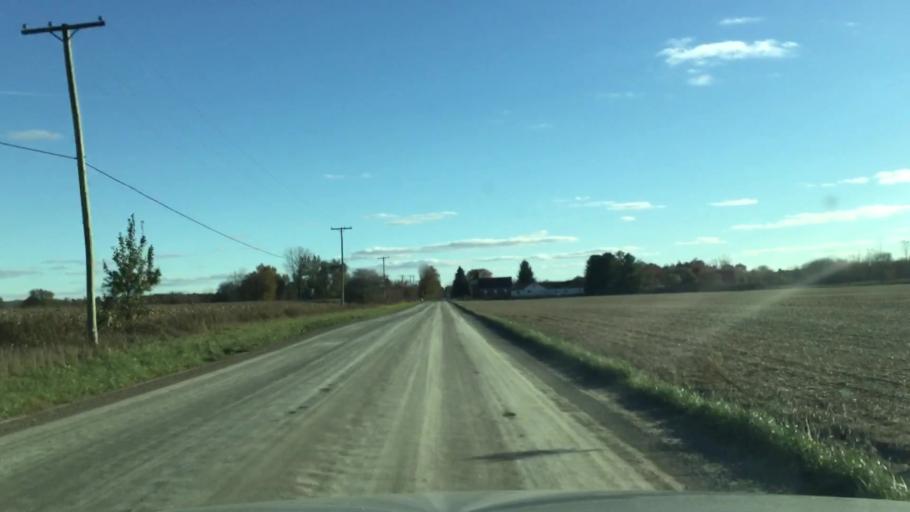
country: US
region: Michigan
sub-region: Lapeer County
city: Lapeer
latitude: 43.0711
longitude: -83.2274
